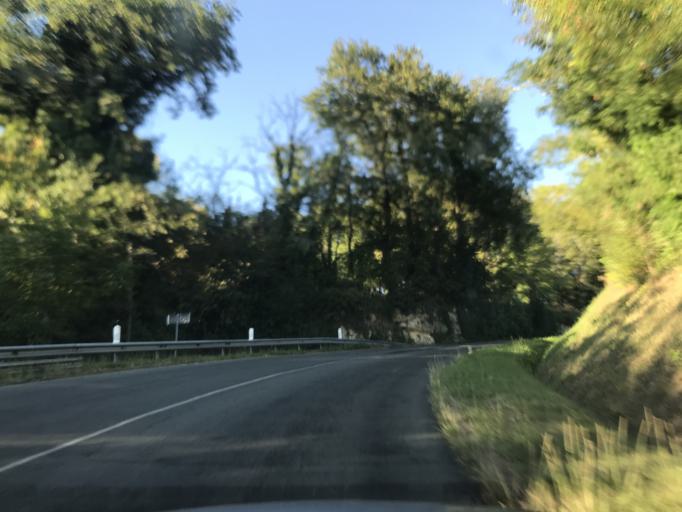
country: FR
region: Aquitaine
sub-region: Departement de la Gironde
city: Rauzan
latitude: 44.7781
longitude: -0.0600
